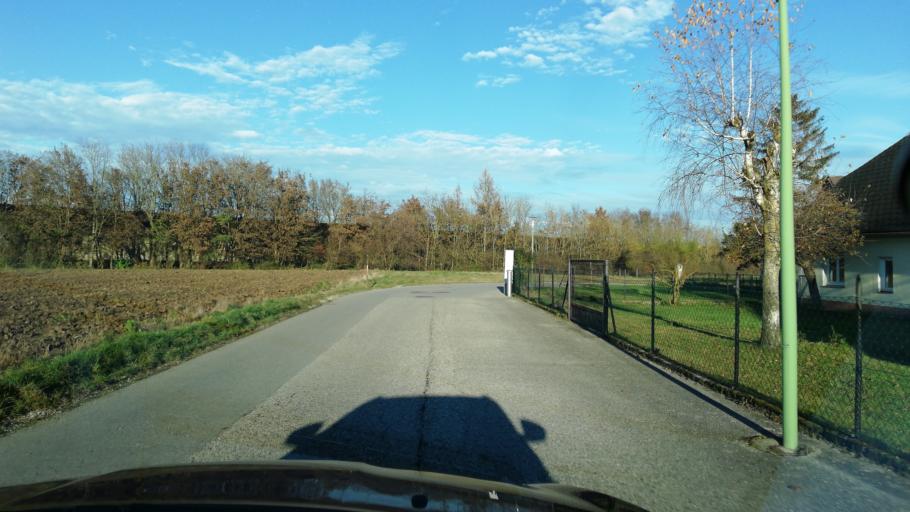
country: AT
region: Upper Austria
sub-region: Wels Stadt
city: Wels
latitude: 48.1907
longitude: 14.0553
